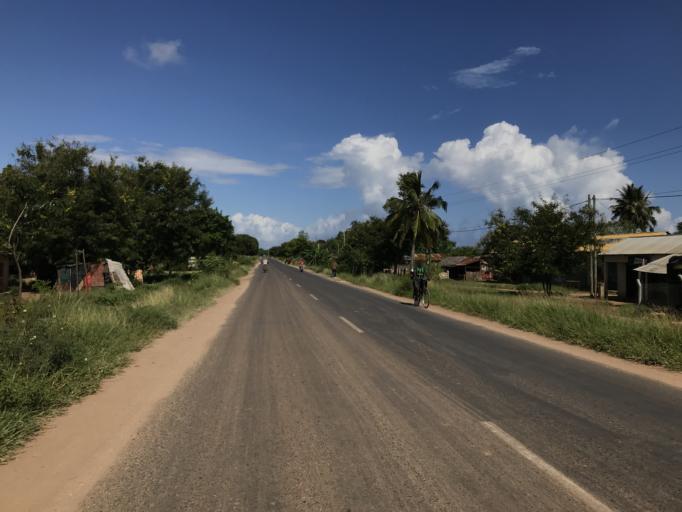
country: TZ
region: Dar es Salaam
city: Dar es Salaam
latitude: -6.8733
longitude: 39.4080
